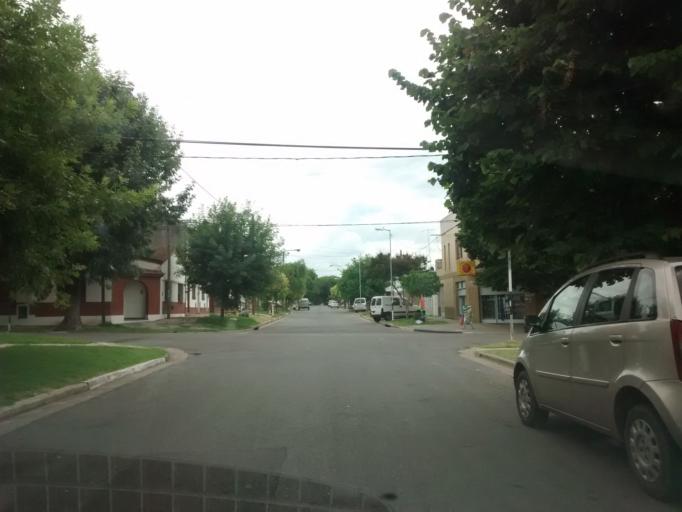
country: AR
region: Buenos Aires
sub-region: Partido de La Plata
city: La Plata
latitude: -34.9288
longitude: -57.9213
